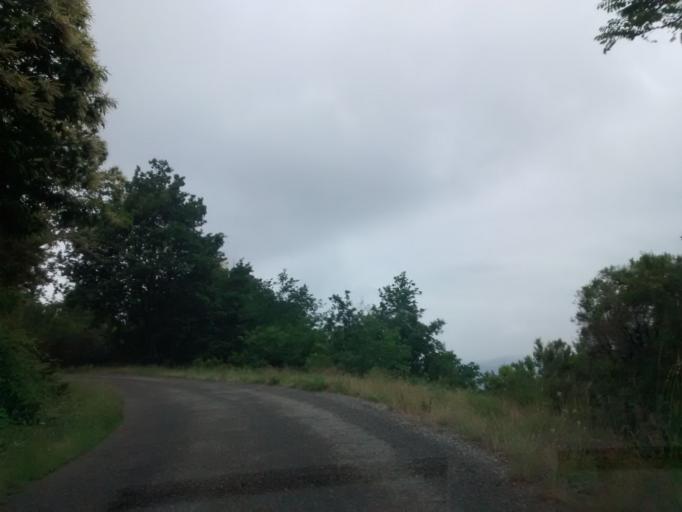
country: ES
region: Galicia
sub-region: Provincia de Ourense
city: Castro Caldelas
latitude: 42.4150
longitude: -7.3889
